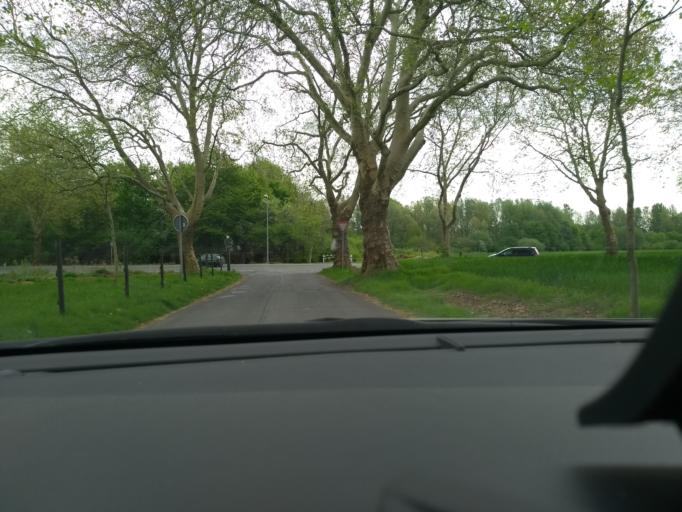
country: DE
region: North Rhine-Westphalia
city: Lunen
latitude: 51.6010
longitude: 7.5217
